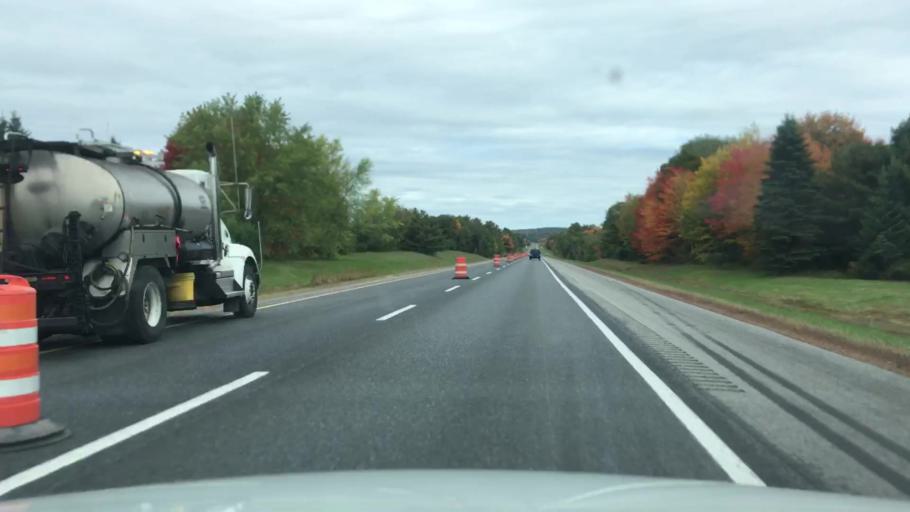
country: US
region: Maine
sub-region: Sagadahoc County
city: Richmond
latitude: 44.1296
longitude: -69.8465
